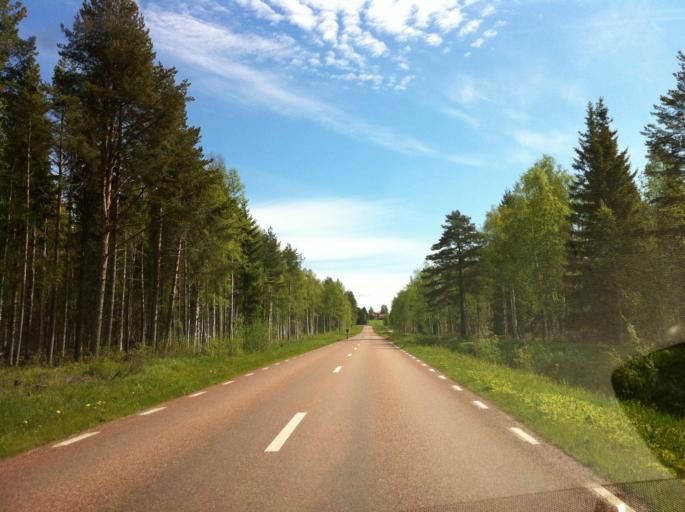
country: SE
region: Dalarna
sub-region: Mora Kommun
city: Mora
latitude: 60.9027
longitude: 14.5932
